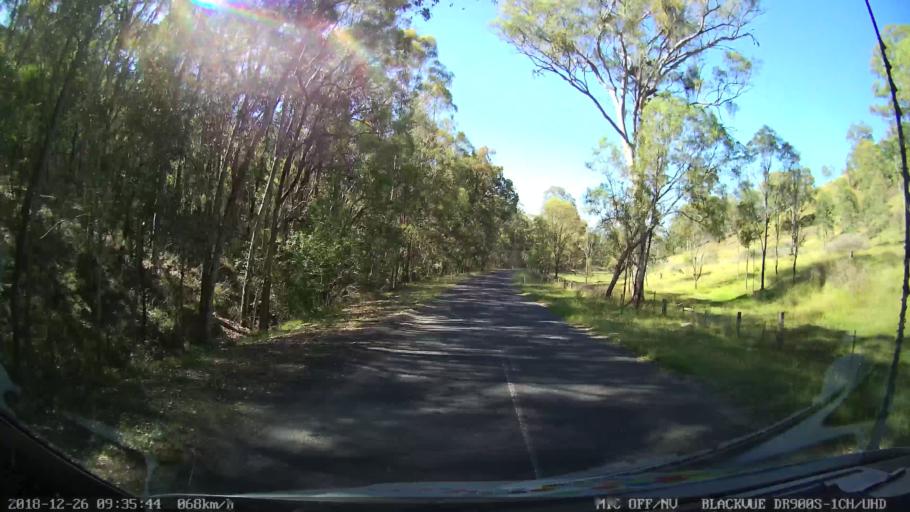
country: AU
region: New South Wales
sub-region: Mid-Western Regional
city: Kandos
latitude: -32.9176
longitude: 150.0415
